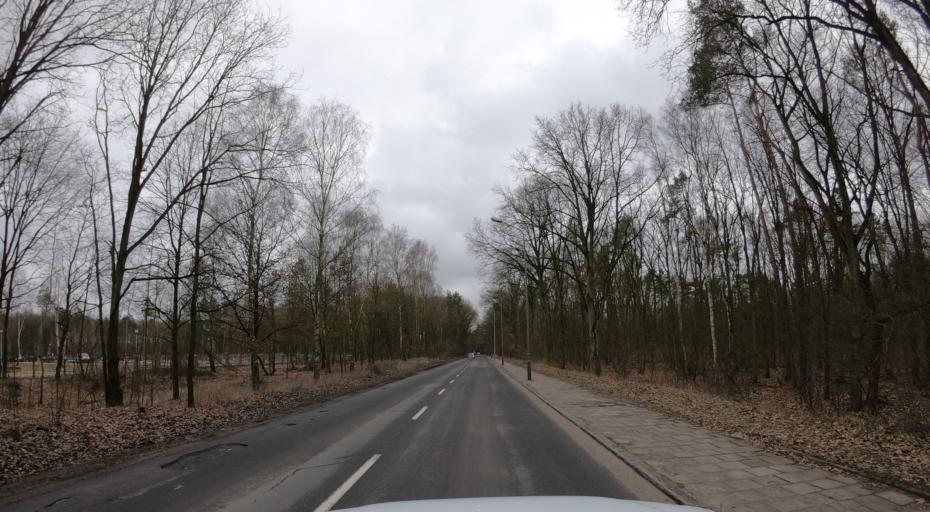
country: PL
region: West Pomeranian Voivodeship
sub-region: Powiat policki
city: Police
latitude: 53.5491
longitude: 14.5471
